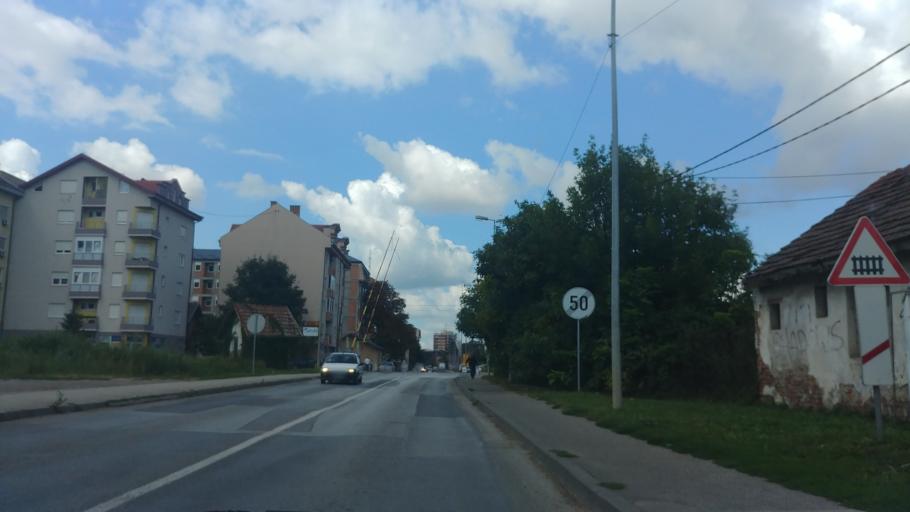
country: BA
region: Brcko
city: Brcko
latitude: 44.8697
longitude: 18.8177
